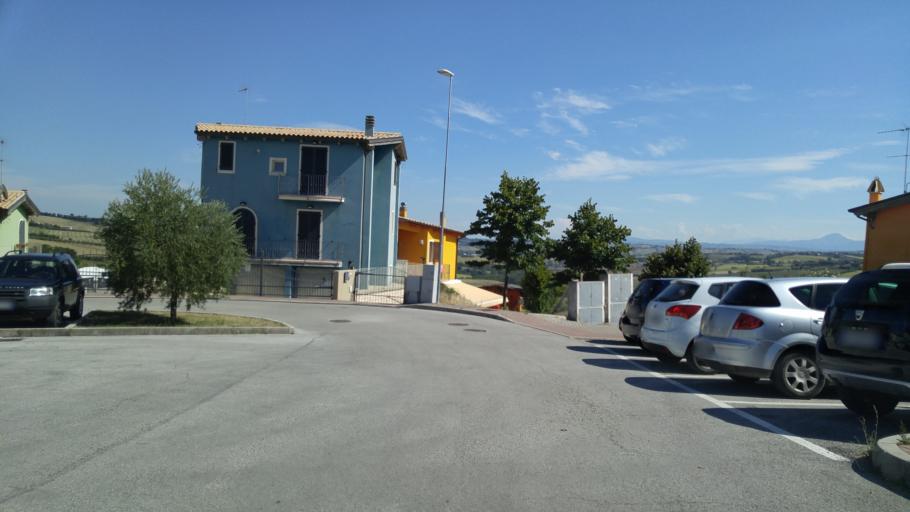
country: IT
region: The Marches
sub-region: Provincia di Pesaro e Urbino
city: San Giorgio di Pesaro
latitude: 43.7083
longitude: 12.9867
